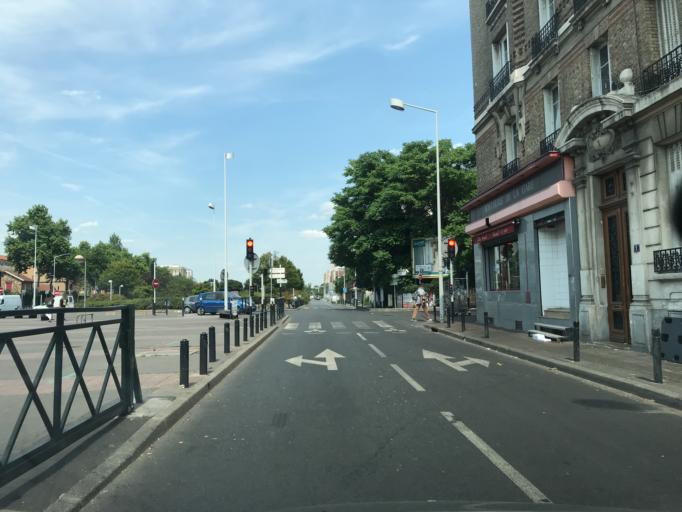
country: FR
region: Ile-de-France
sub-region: Departement des Hauts-de-Seine
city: Nanterre
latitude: 48.8962
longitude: 2.1958
